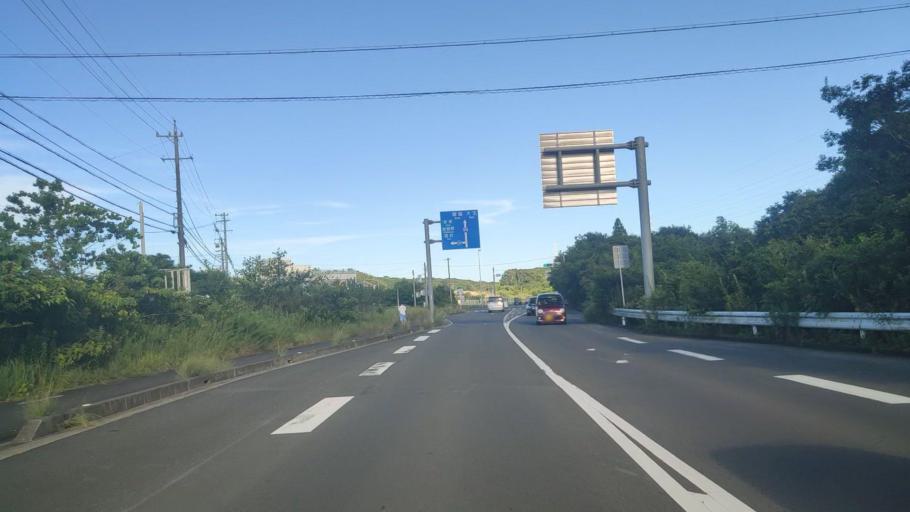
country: JP
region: Mie
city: Toba
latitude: 34.3311
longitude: 136.8410
